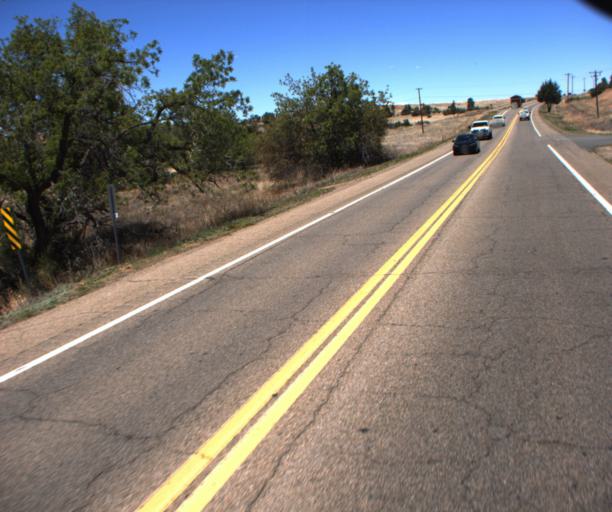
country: US
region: Arizona
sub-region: Yavapai County
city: Prescott
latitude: 34.6220
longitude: -112.4256
